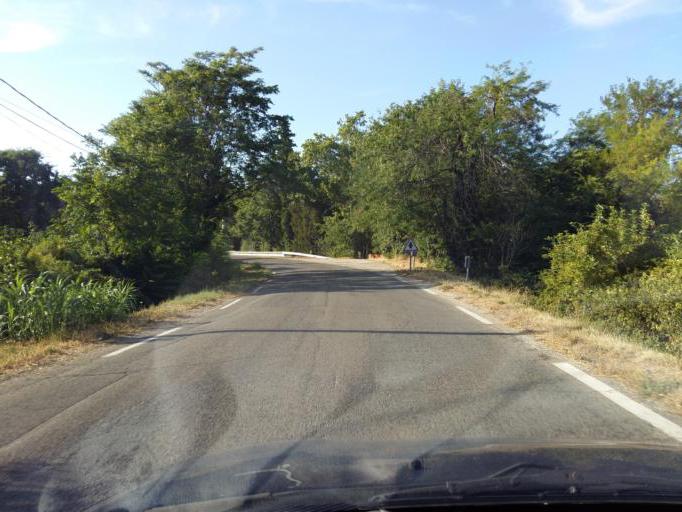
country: FR
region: Provence-Alpes-Cote d'Azur
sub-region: Departement du Vaucluse
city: Saint-Didier
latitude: 44.0145
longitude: 5.1027
